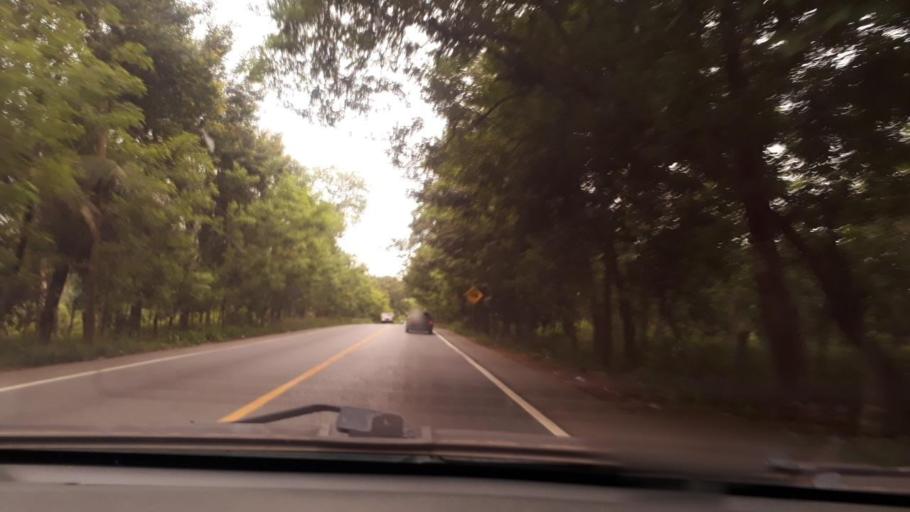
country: GT
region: Izabal
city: Morales
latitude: 15.4947
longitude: -88.8569
